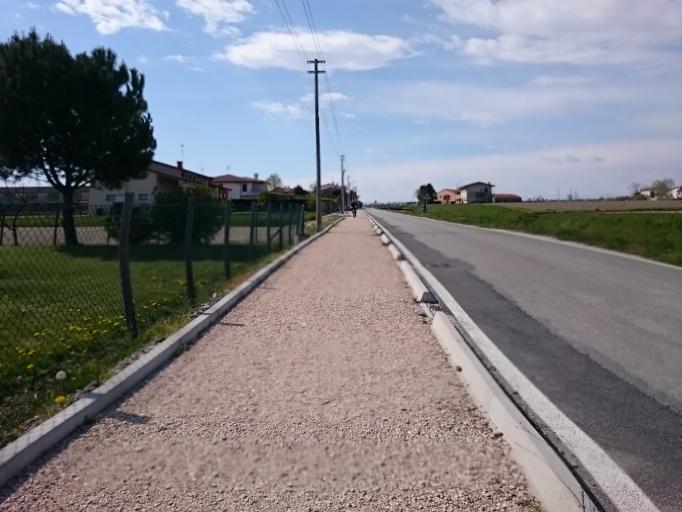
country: IT
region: Veneto
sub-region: Provincia di Padova
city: Polverara
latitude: 45.3177
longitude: 11.9568
